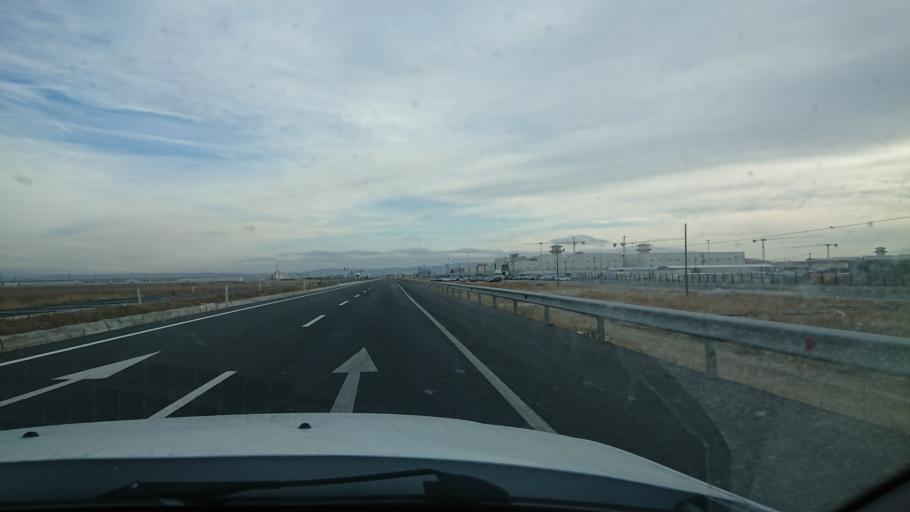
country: TR
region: Aksaray
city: Aksaray
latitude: 38.3341
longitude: 33.9229
